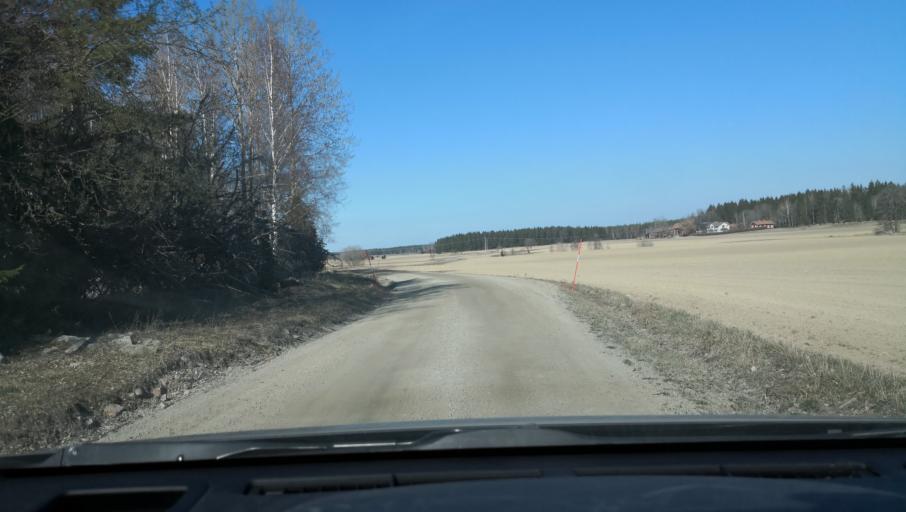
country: SE
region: Vaestmanland
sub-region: Sala Kommun
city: Sala
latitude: 59.8891
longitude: 16.5274
